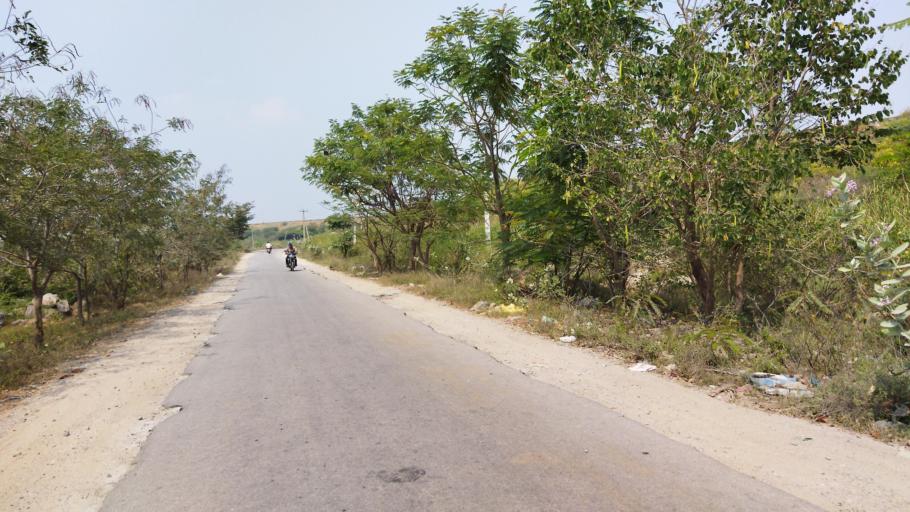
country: IN
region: Telangana
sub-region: Nalgonda
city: Nalgonda
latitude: 17.0742
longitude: 79.3150
